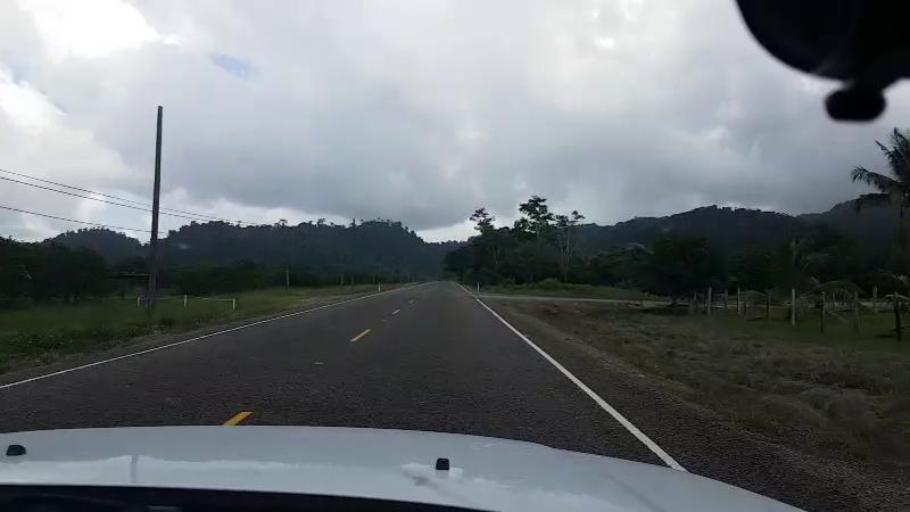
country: BZ
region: Cayo
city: Belmopan
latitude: 17.1482
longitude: -88.7063
